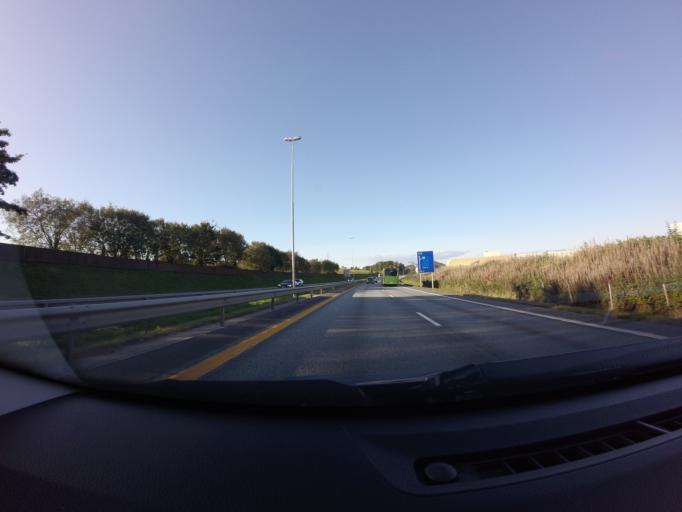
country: NO
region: Rogaland
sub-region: Sandnes
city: Sandnes
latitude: 58.8785
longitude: 5.7182
